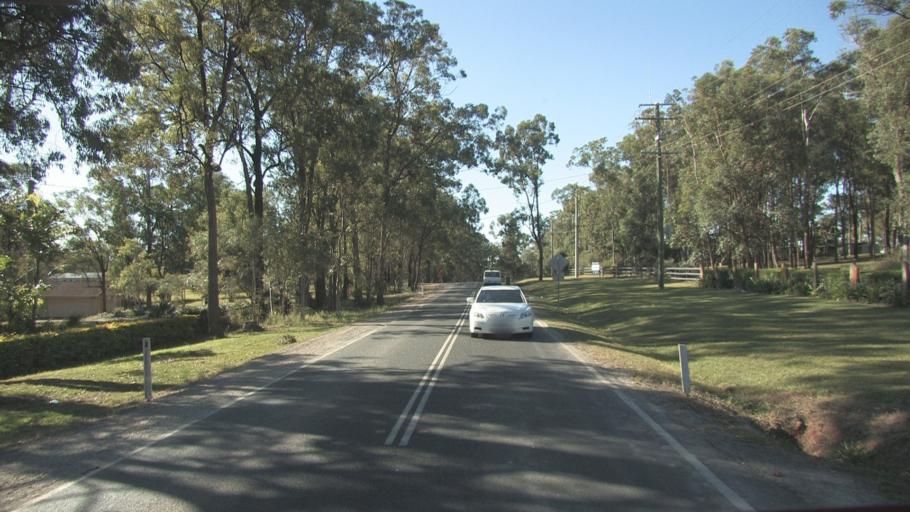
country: AU
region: Queensland
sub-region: Logan
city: Waterford West
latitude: -27.7436
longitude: 153.1428
